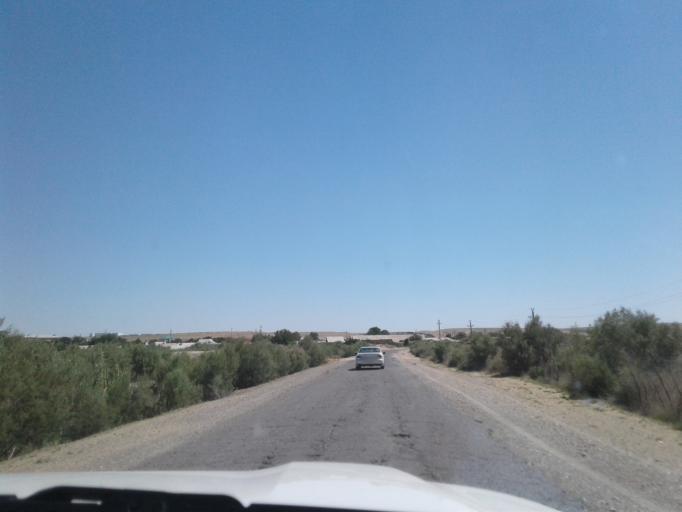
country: AF
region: Badghis
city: Bala Murghab
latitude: 35.9613
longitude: 62.9073
